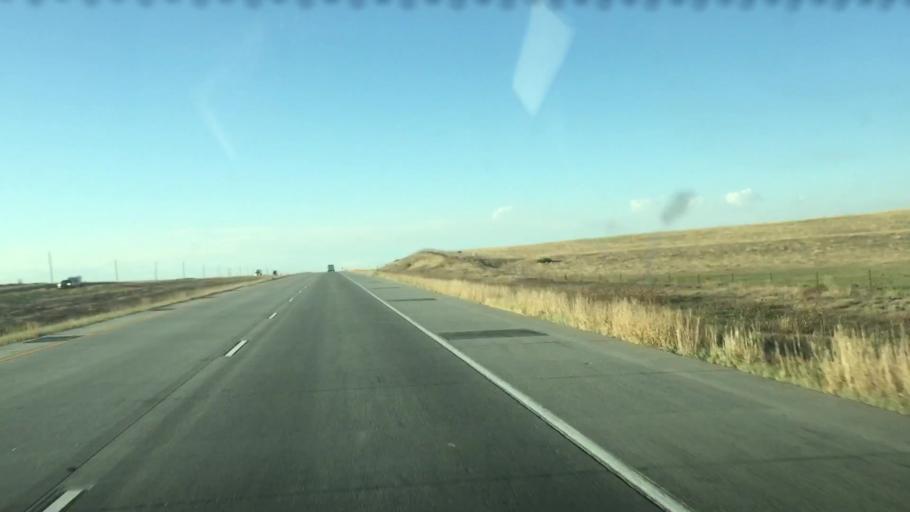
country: US
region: Colorado
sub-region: Arapahoe County
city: Byers
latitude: 39.5758
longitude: -104.0201
